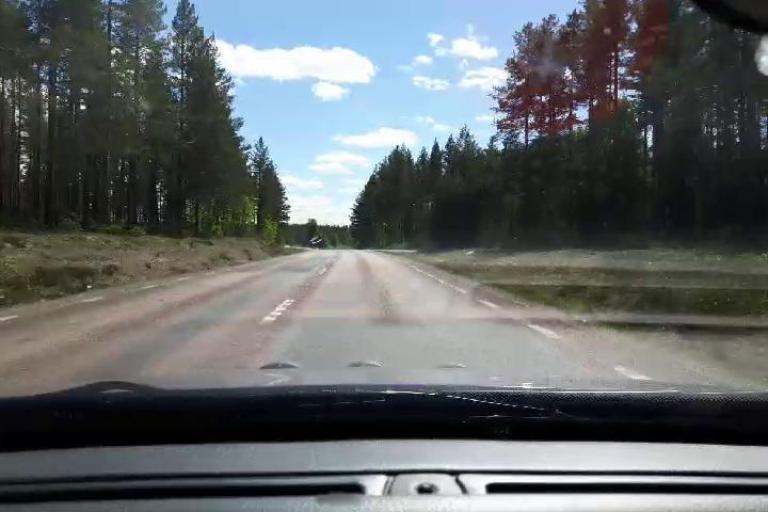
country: SE
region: Gaevleborg
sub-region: Ljusdals Kommun
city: Farila
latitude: 61.8434
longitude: 15.7507
